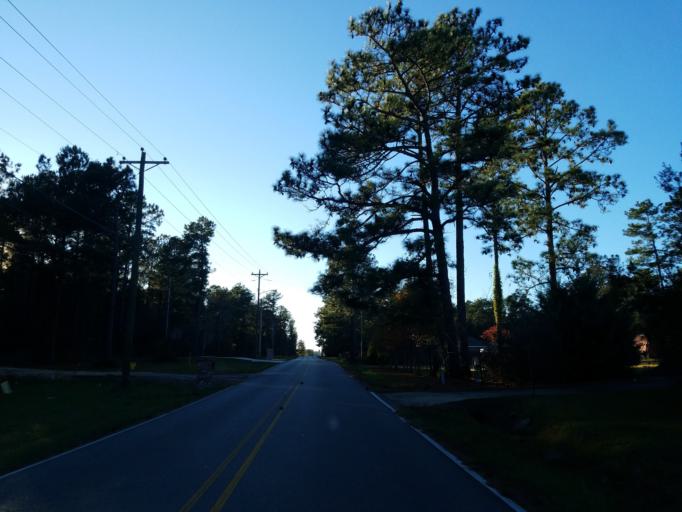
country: US
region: Mississippi
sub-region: Lamar County
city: Arnold Line
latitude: 31.3467
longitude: -89.3853
